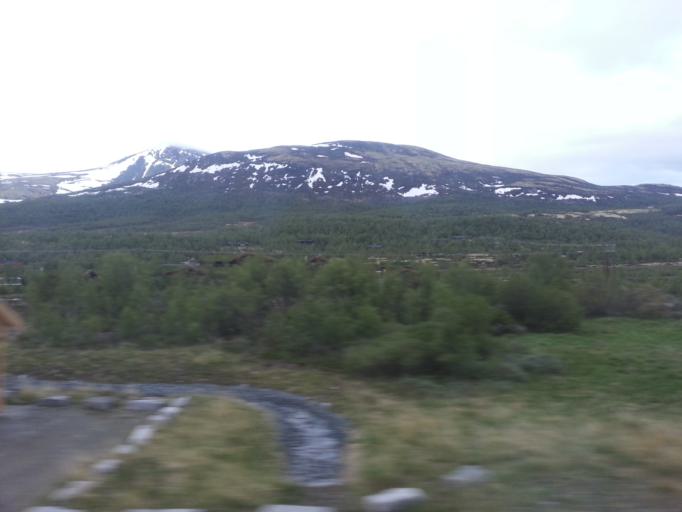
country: NO
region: Oppland
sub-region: Dovre
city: Dovre
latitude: 62.1758
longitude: 9.4293
